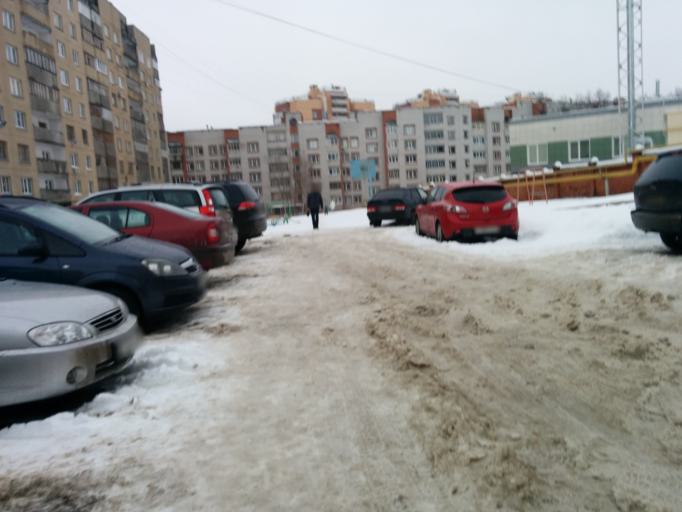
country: RU
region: Chuvashia
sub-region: Cheboksarskiy Rayon
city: Cheboksary
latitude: 56.1453
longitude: 47.2327
